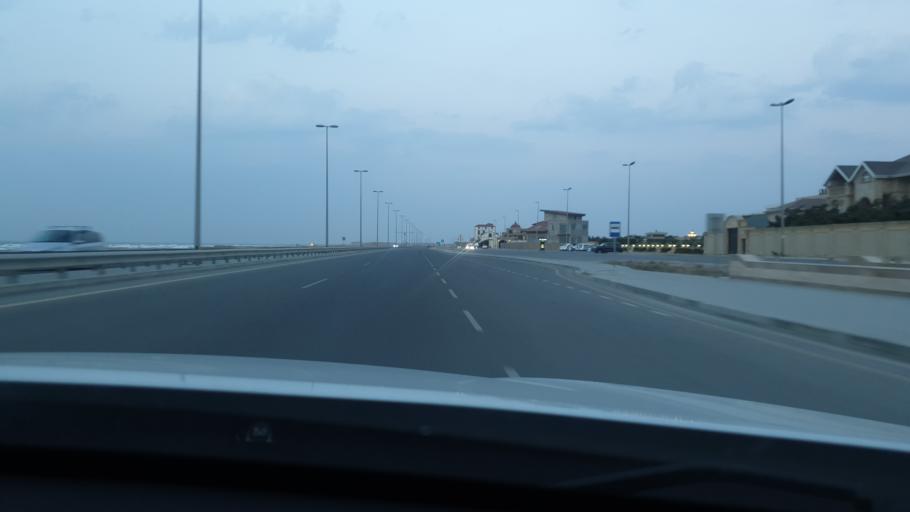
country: AZ
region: Baki
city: Bilajer
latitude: 40.5874
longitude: 50.0408
